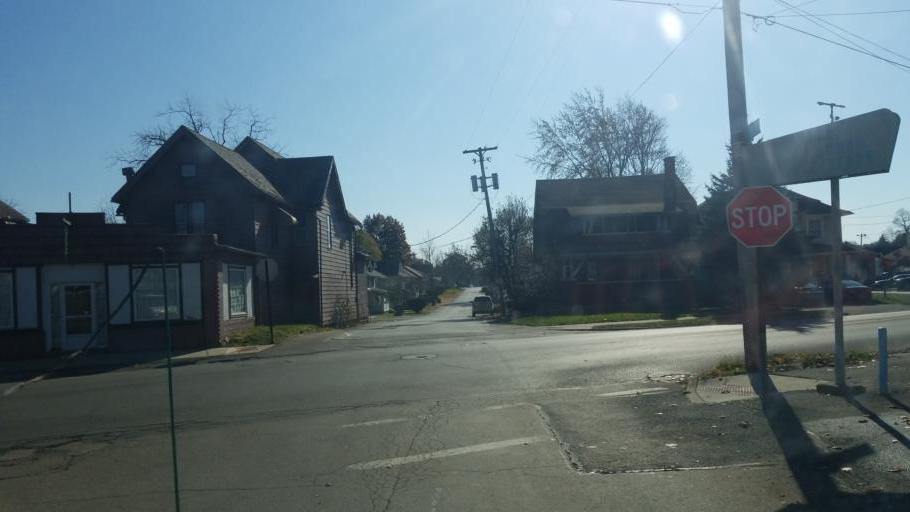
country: US
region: Ohio
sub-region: Richland County
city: Mansfield
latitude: 40.7560
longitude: -82.5326
